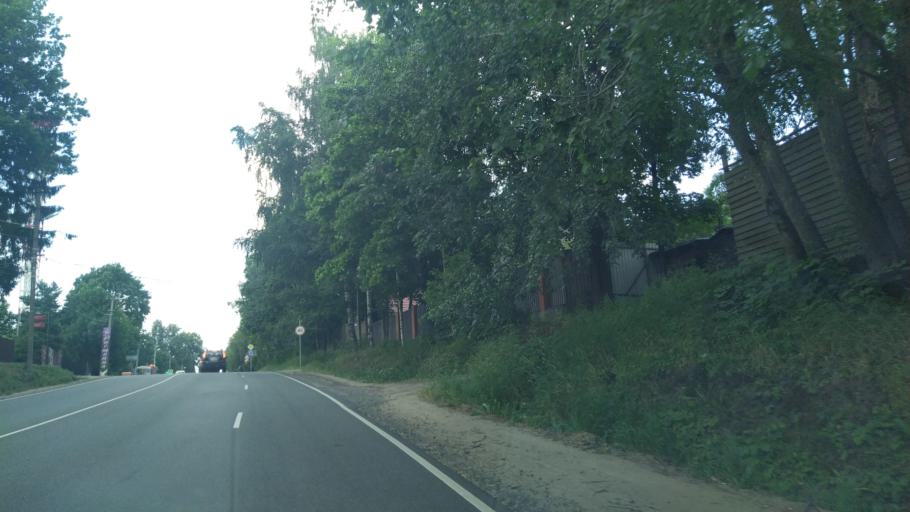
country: RU
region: Leningrad
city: Toksovo
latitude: 60.1593
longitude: 30.5350
